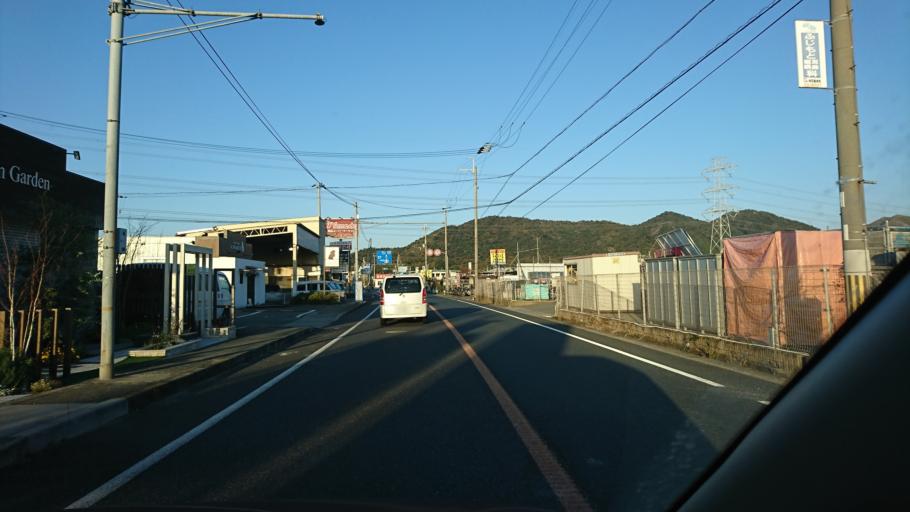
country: JP
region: Hyogo
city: Kakogawacho-honmachi
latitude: 34.7949
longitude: 134.7859
